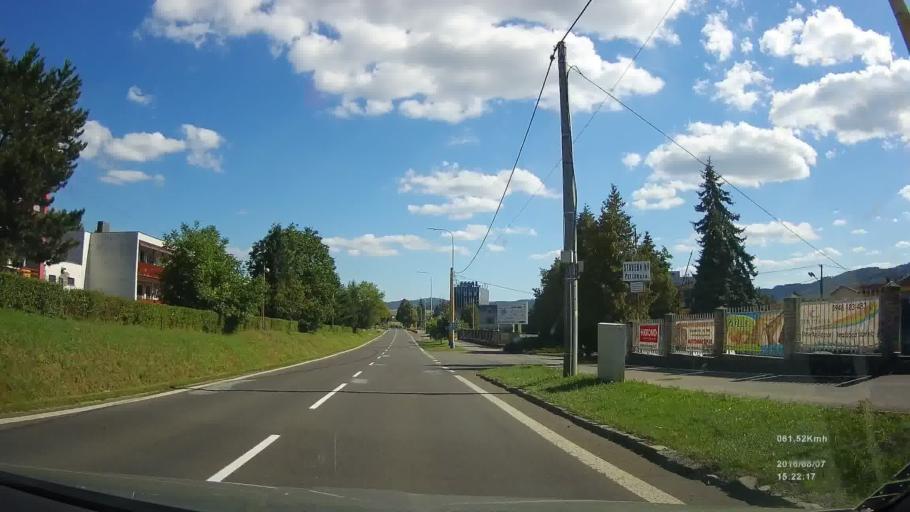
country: SK
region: Presovsky
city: Stropkov
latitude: 49.1938
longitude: 21.6551
